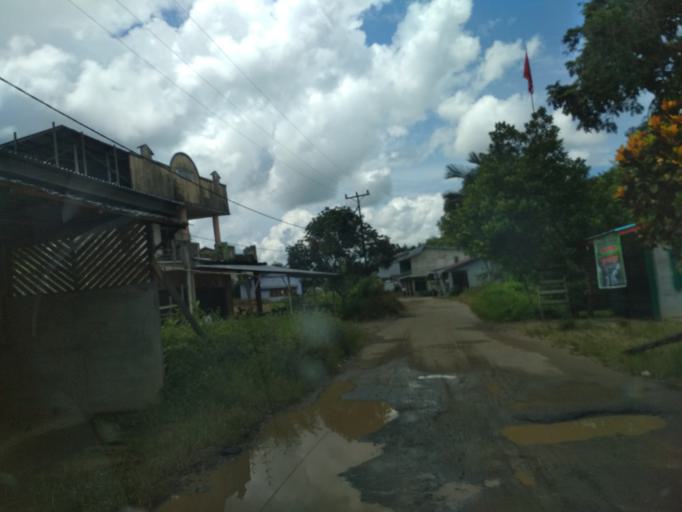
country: ID
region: West Kalimantan
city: Bengkayang
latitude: 0.7477
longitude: 110.1114
